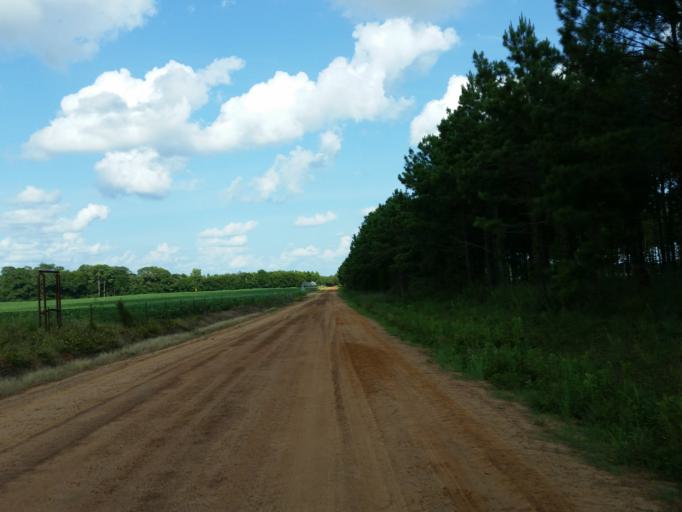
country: US
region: Georgia
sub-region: Lee County
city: Leesburg
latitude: 31.8742
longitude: -84.0603
